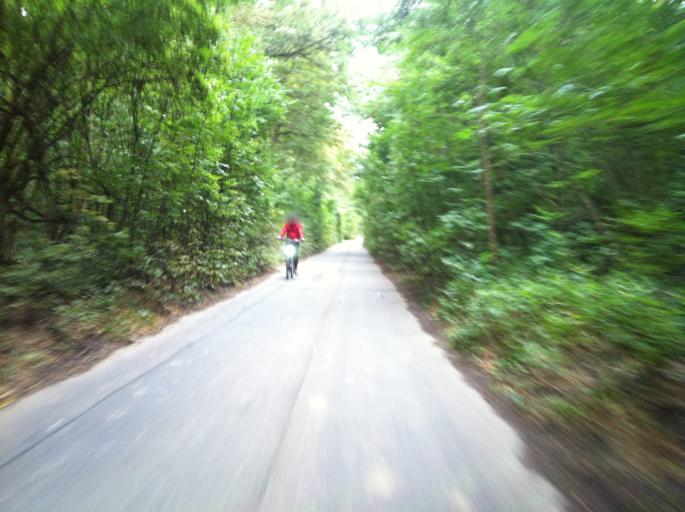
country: DE
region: Rheinland-Pfalz
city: Essenheim
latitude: 49.9546
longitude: 8.1640
